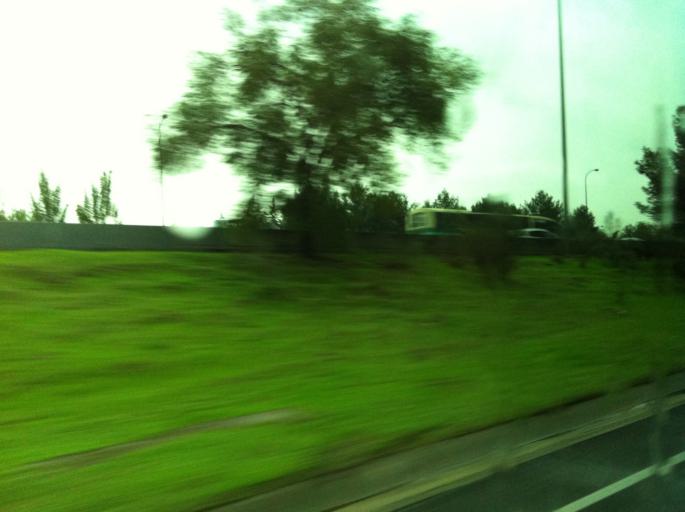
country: ES
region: Madrid
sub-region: Provincia de Madrid
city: Puente de Vallecas
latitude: 40.3919
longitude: -3.6776
